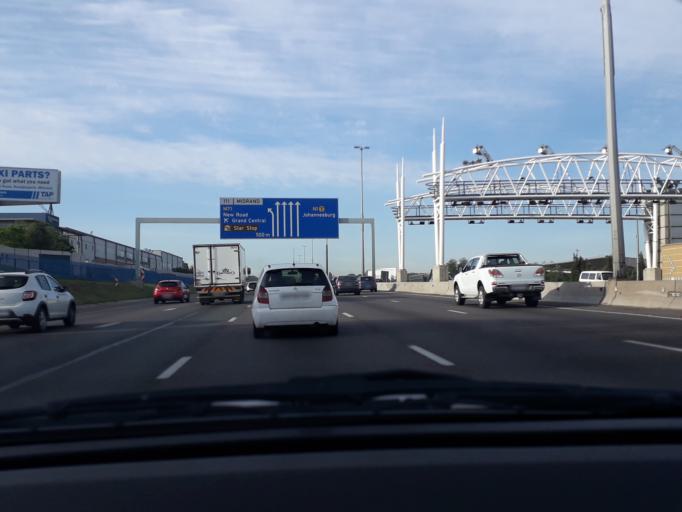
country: ZA
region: Gauteng
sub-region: City of Johannesburg Metropolitan Municipality
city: Midrand
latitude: -25.9699
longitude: 28.1296
